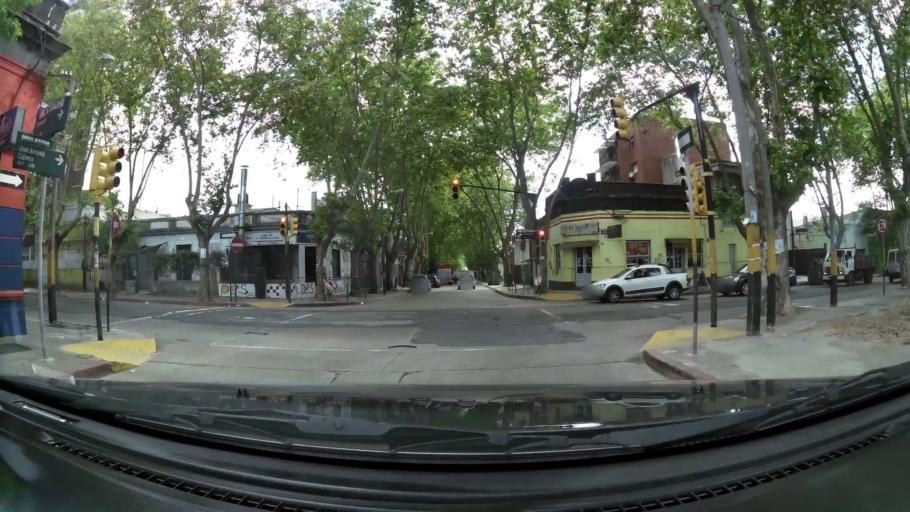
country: UY
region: Montevideo
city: Montevideo
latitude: -34.8777
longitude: -56.1416
